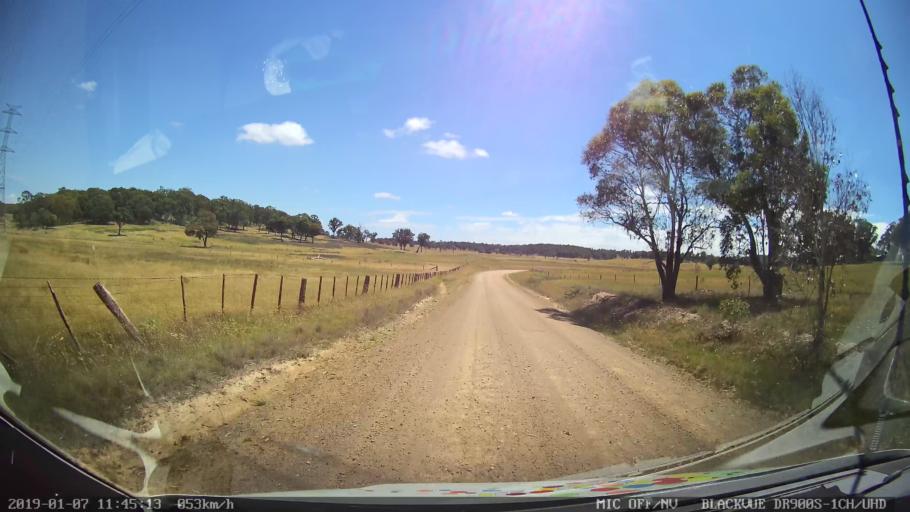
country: AU
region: New South Wales
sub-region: Guyra
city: Guyra
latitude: -30.3475
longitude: 151.6051
